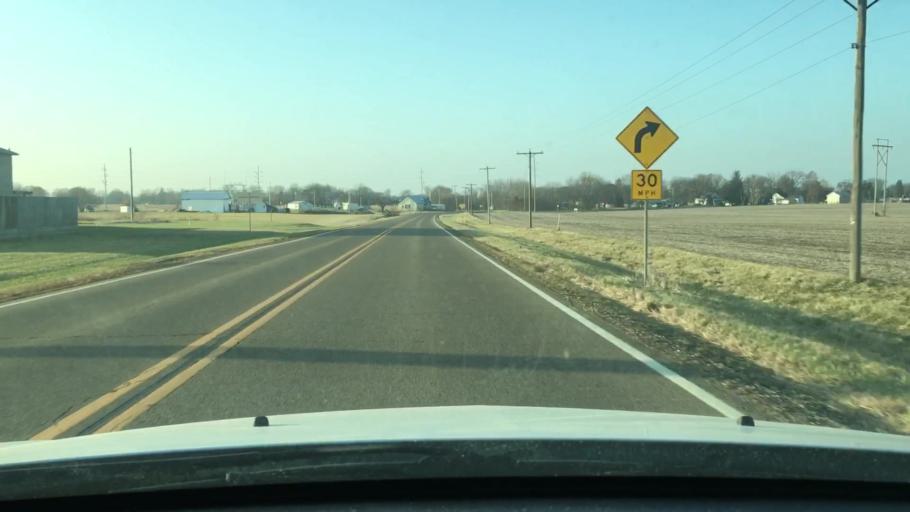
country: US
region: Illinois
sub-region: Woodford County
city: Washburn
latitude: 40.9275
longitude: -89.2833
